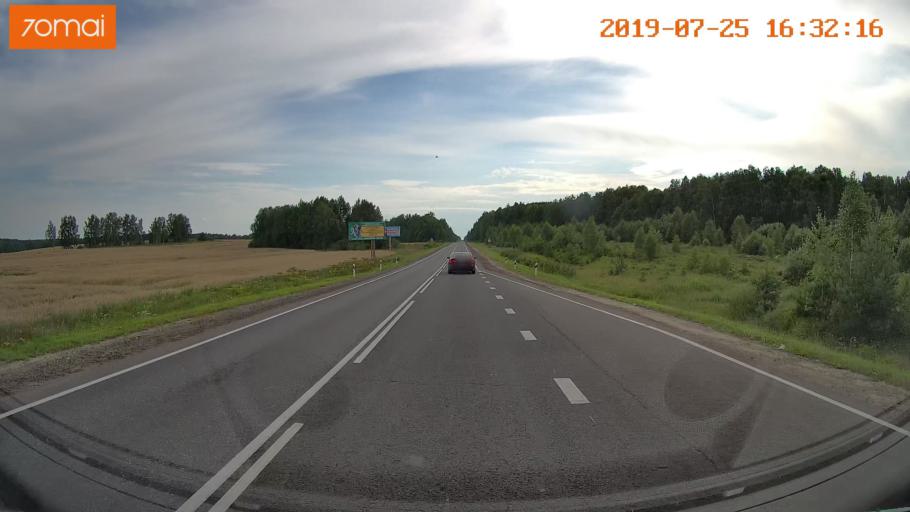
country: RU
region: Ivanovo
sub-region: Privolzhskiy Rayon
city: Ples
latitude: 57.4379
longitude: 41.4765
